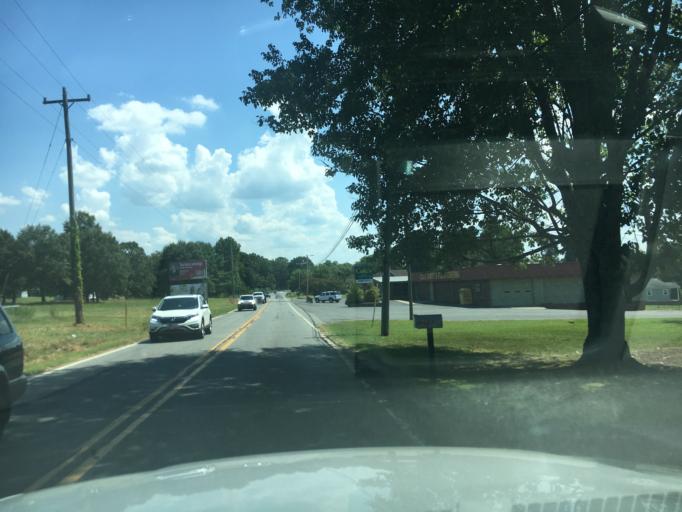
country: US
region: North Carolina
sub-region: Rutherford County
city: Forest City
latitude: 35.2883
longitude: -81.8437
